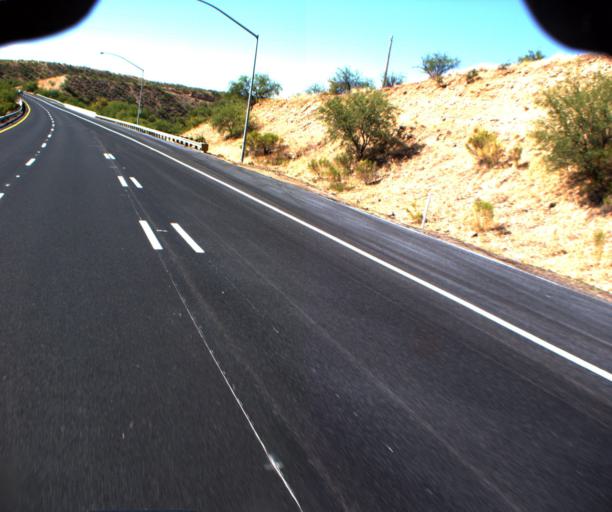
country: US
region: Arizona
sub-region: Santa Cruz County
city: Tubac
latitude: 31.5521
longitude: -111.0499
